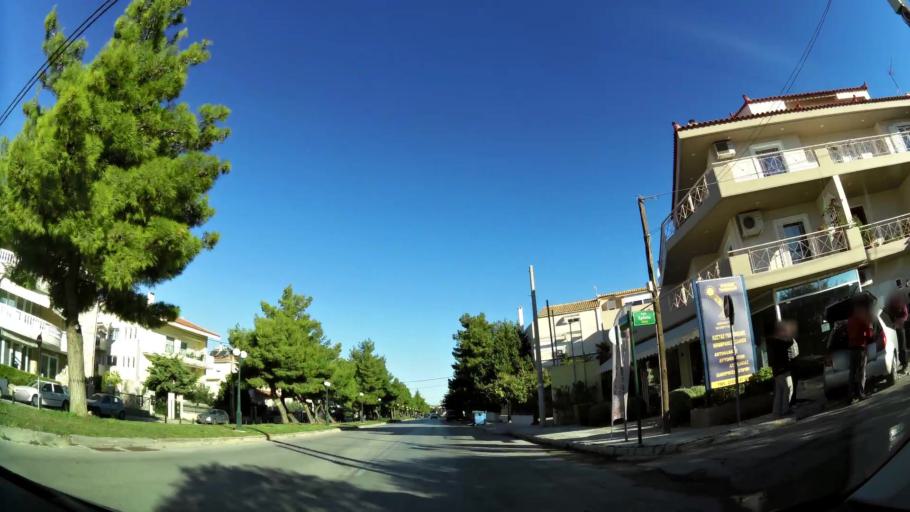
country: GR
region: Attica
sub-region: Nomarchia Anatolikis Attikis
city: Gerakas
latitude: 38.0158
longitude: 23.8529
